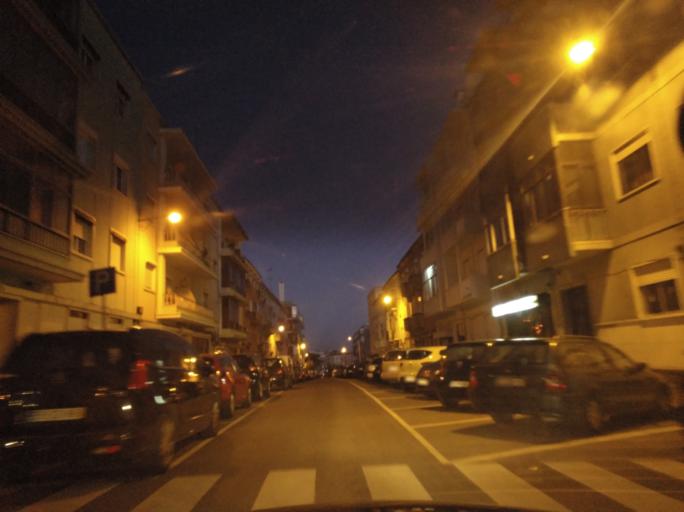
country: PT
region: Lisbon
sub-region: Oeiras
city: Alges
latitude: 38.7047
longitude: -9.1959
